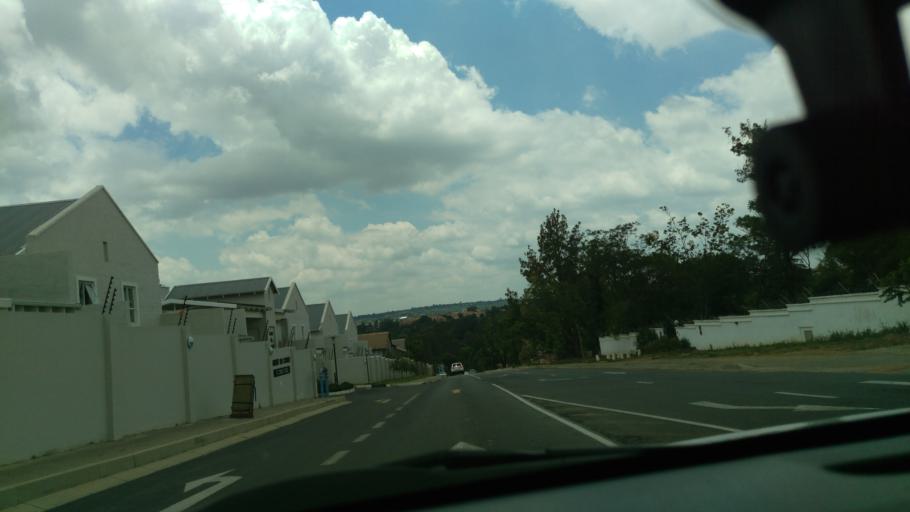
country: ZA
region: Gauteng
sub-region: City of Johannesburg Metropolitan Municipality
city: Midrand
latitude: -26.0416
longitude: 28.0457
